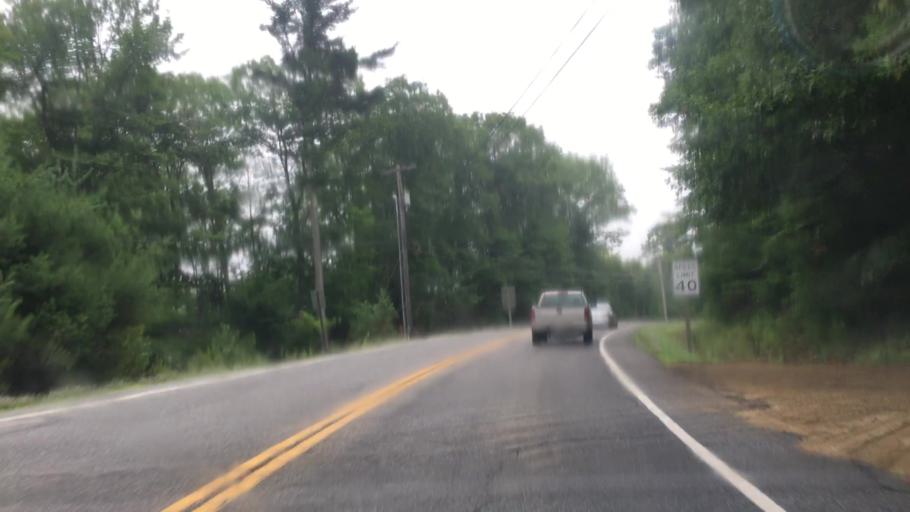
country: US
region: Maine
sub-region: Lincoln County
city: Wiscasset
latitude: 43.9990
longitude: -69.6320
